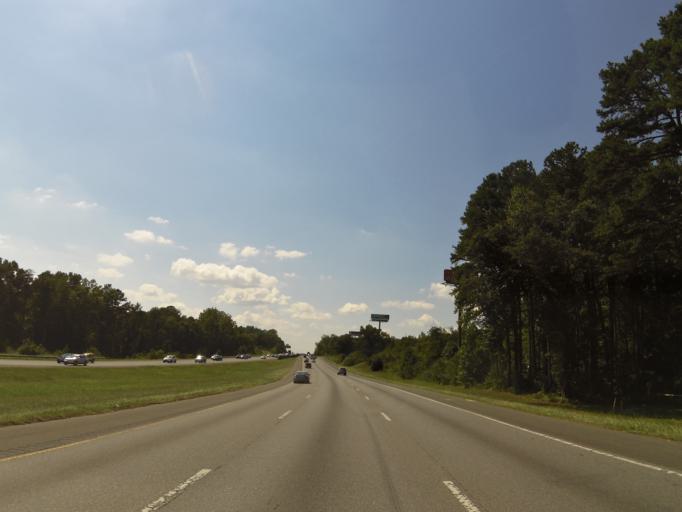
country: US
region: North Carolina
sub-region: Gaston County
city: Cramerton
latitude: 35.2641
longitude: -81.0595
